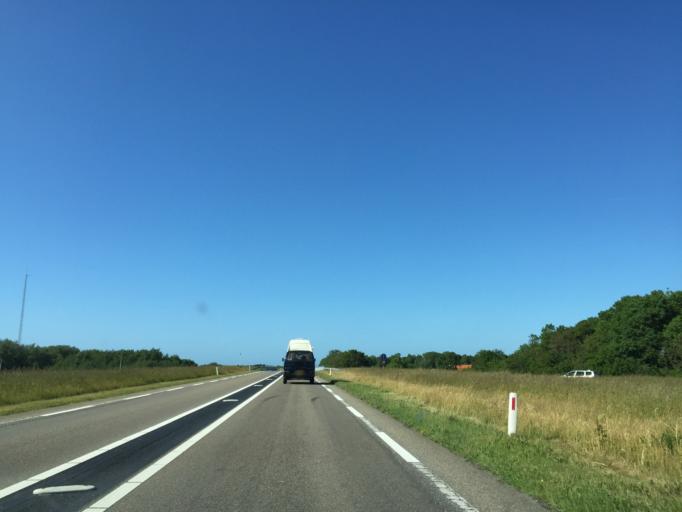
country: NL
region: Zeeland
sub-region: Schouwen-Duiveland
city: Scharendijke
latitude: 51.7325
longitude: 3.8243
